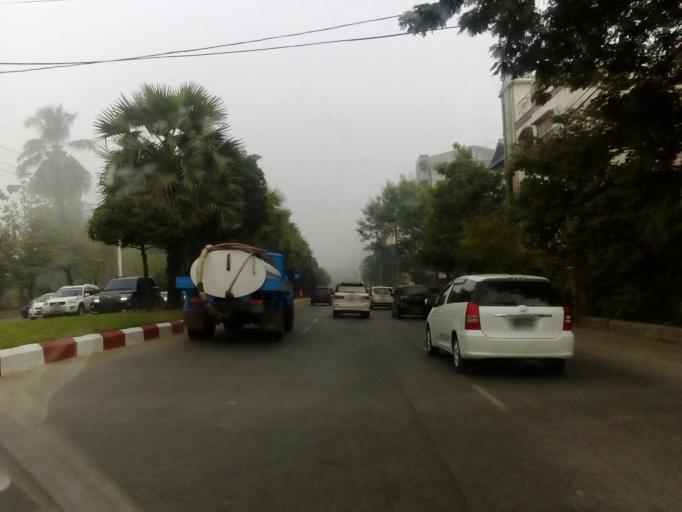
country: MM
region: Yangon
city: Yangon
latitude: 16.8285
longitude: 96.1799
